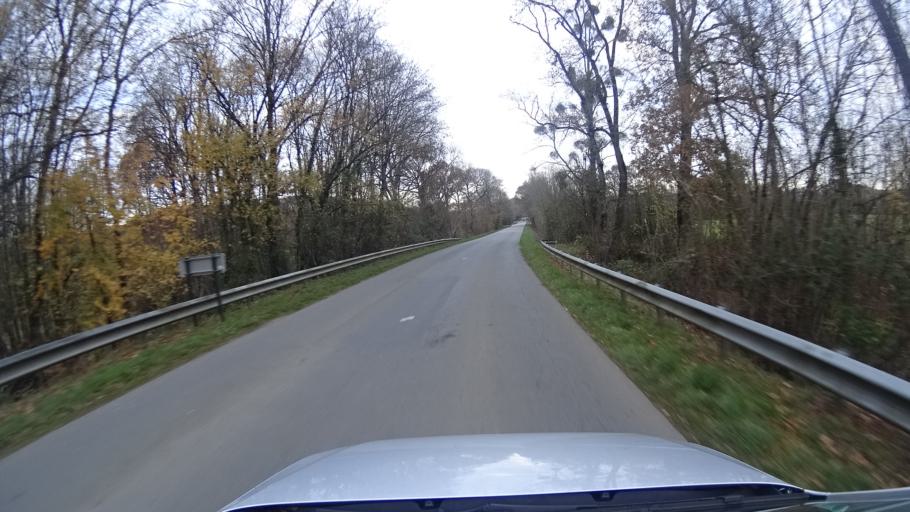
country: FR
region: Brittany
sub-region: Departement d'Ille-et-Vilaine
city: Langon
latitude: 47.7024
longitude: -1.8692
